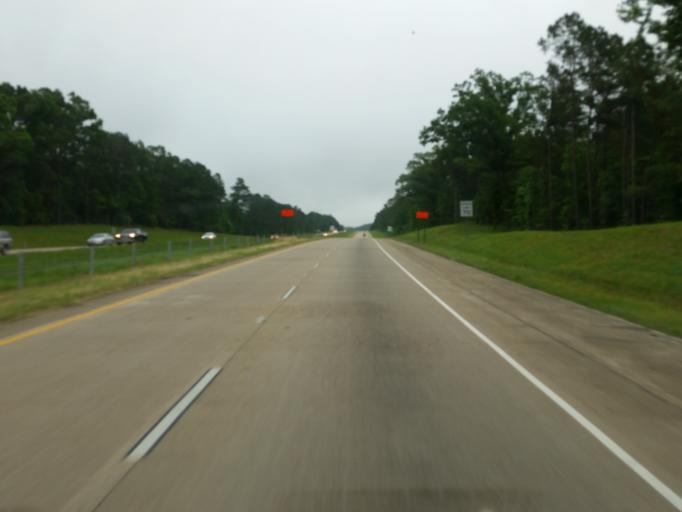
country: US
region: Louisiana
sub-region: Bienville Parish
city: Arcadia
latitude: 32.5630
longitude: -93.0463
